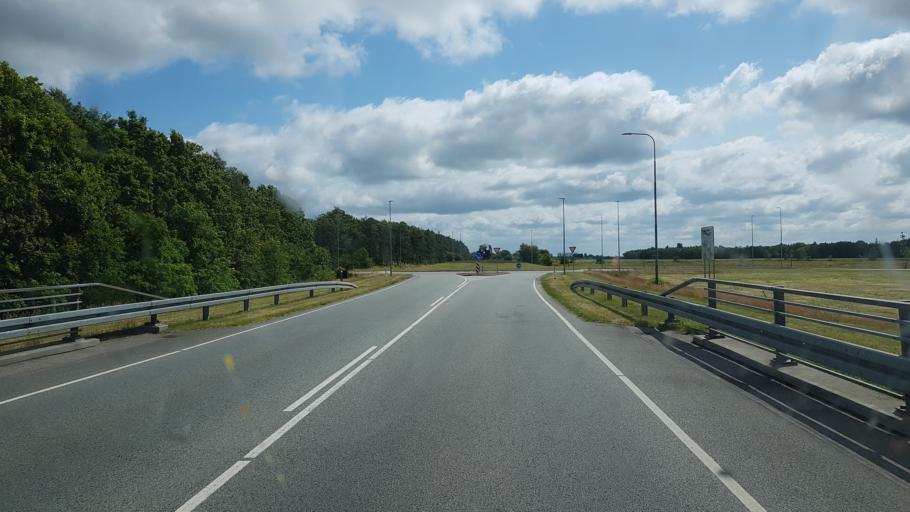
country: DK
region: South Denmark
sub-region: Billund Kommune
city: Grindsted
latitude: 55.7556
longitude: 8.9026
